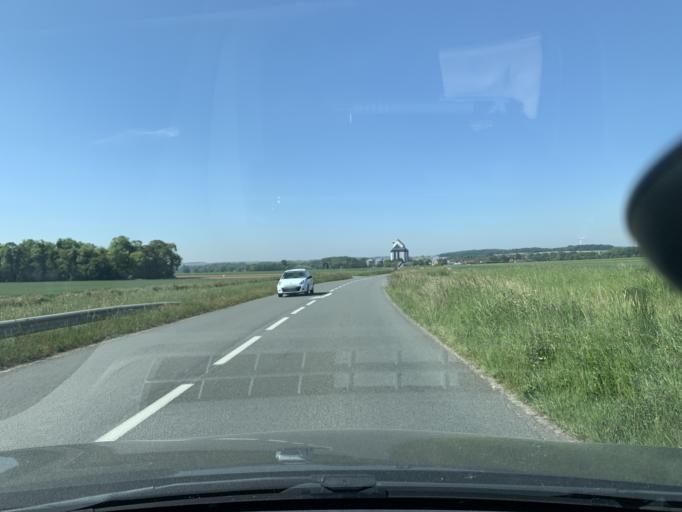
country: FR
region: Nord-Pas-de-Calais
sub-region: Departement du Nord
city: Proville
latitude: 50.1469
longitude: 3.2009
